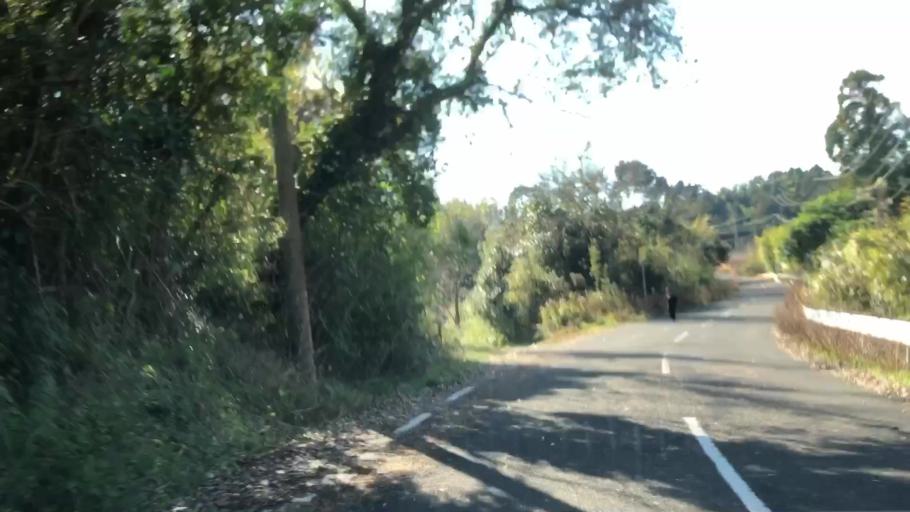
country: JP
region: Kagoshima
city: Satsumasendai
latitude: 31.8610
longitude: 130.3950
